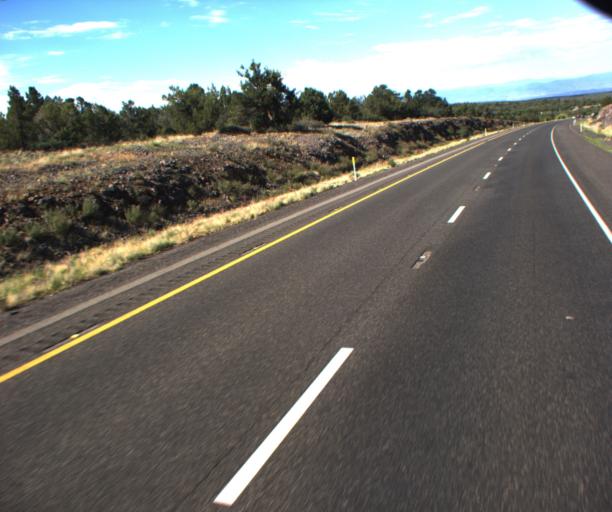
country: US
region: Arizona
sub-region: Yavapai County
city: Village of Oak Creek (Big Park)
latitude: 34.7860
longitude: -111.6077
